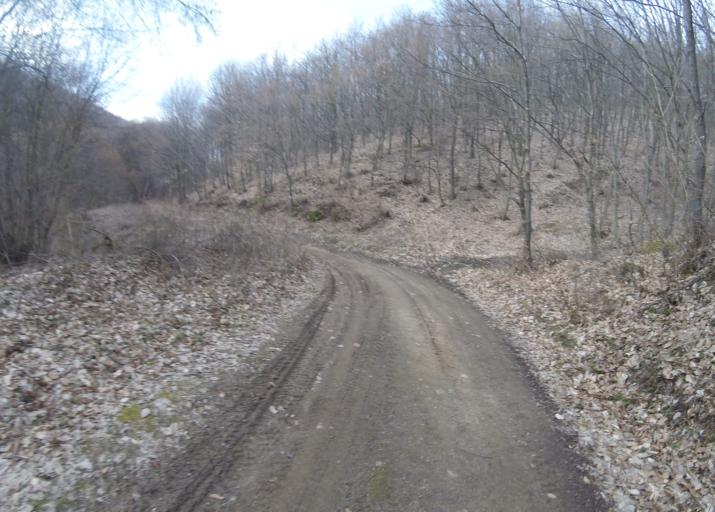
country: HU
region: Heves
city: Belapatfalva
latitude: 48.0331
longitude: 20.3552
